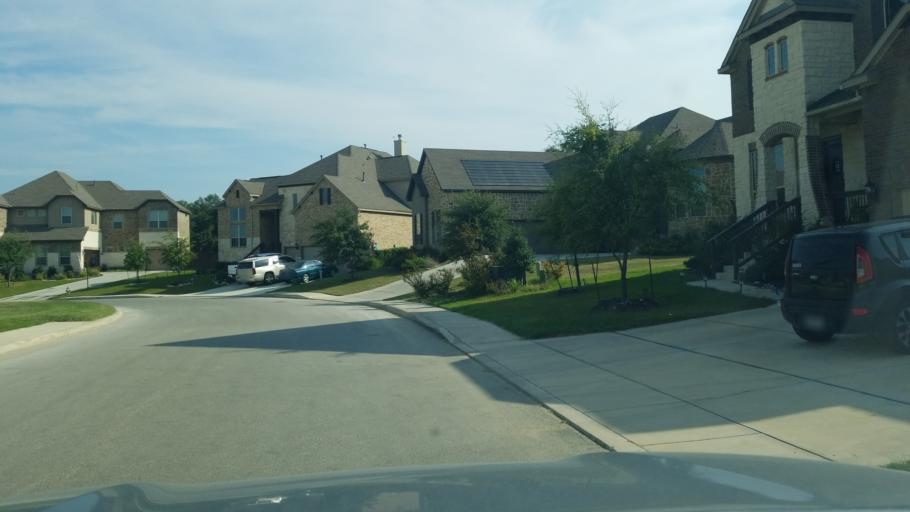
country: US
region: Texas
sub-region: Bexar County
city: Scenic Oaks
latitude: 29.6950
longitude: -98.6396
